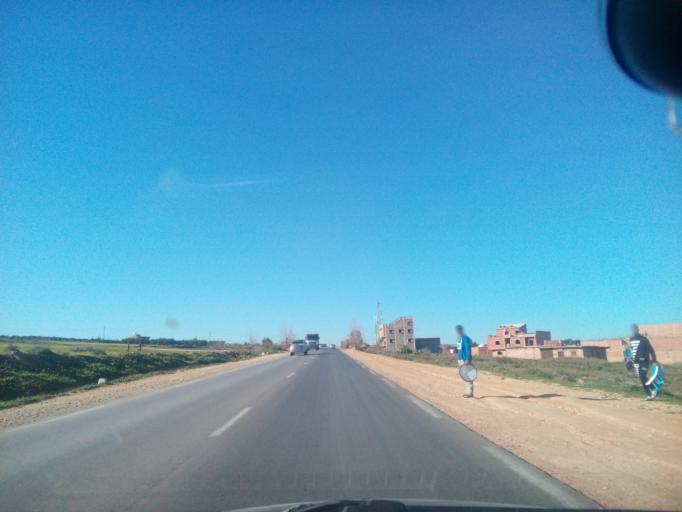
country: DZ
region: Relizane
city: Relizane
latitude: 35.9076
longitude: 0.5096
